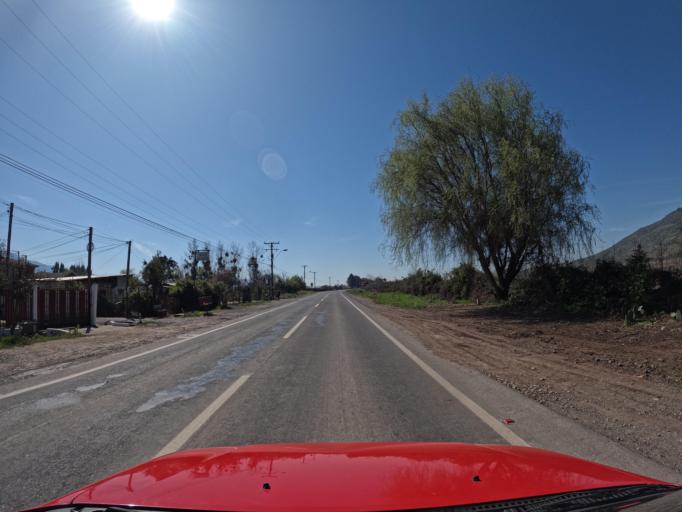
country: CL
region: Maule
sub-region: Provincia de Curico
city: Rauco
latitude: -35.0113
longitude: -71.4163
